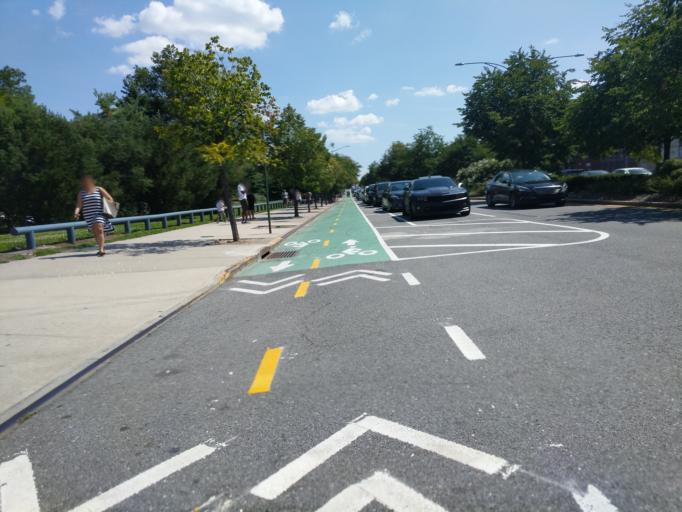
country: US
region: New York
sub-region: Queens County
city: Borough of Queens
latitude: 40.7475
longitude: -73.8535
